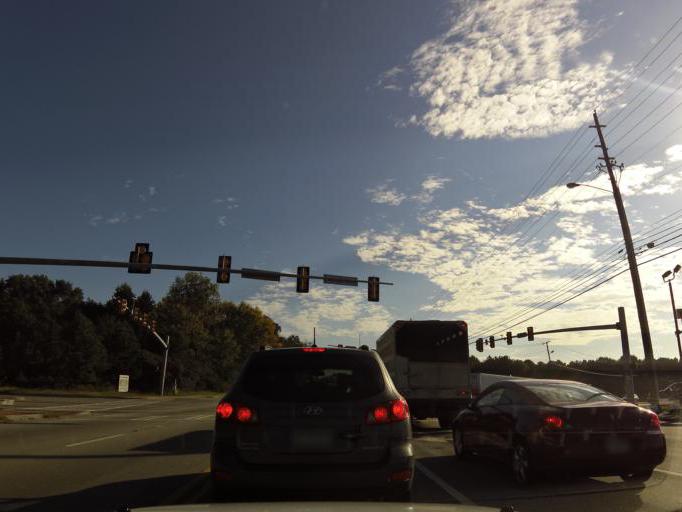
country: US
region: Georgia
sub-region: Cobb County
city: Powder Springs
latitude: 33.8675
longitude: -84.6314
